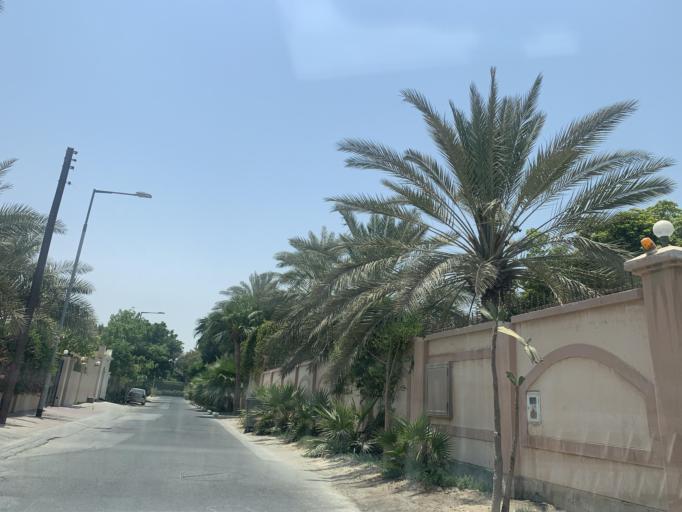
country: BH
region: Manama
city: Jidd Hafs
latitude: 26.2075
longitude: 50.4740
